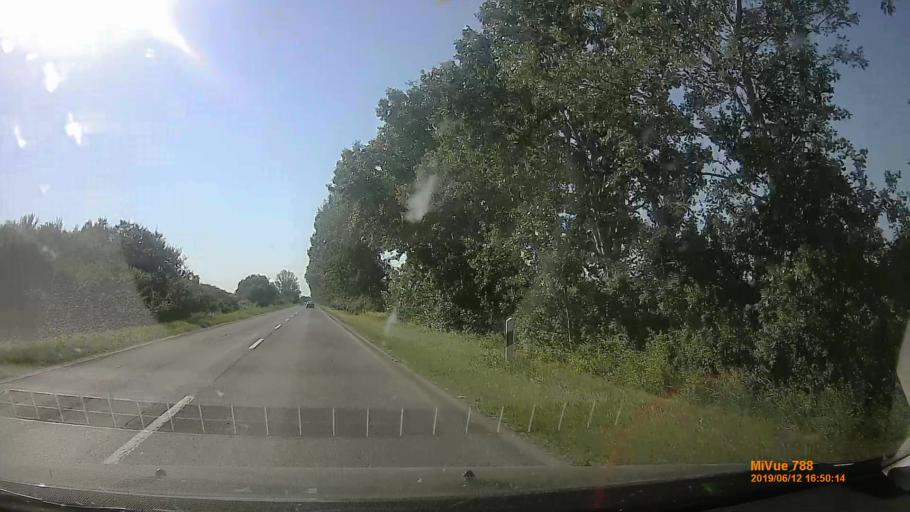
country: HU
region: Csongrad
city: Kiszombor
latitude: 46.1982
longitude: 20.3980
